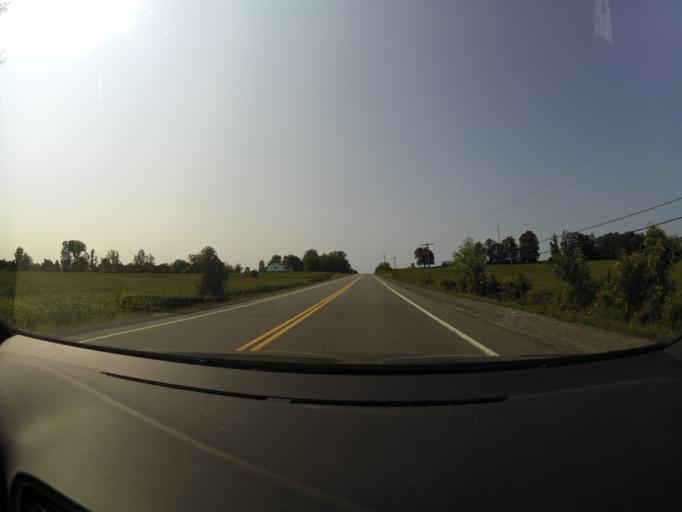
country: CA
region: Ontario
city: Arnprior
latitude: 45.4728
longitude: -76.1769
